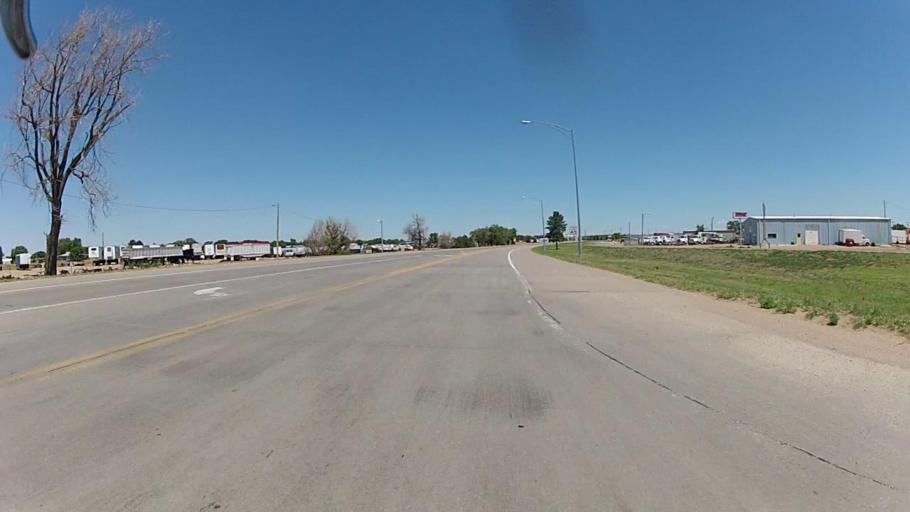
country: US
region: Kansas
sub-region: Ford County
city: Dodge City
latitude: 37.7292
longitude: -100.0184
